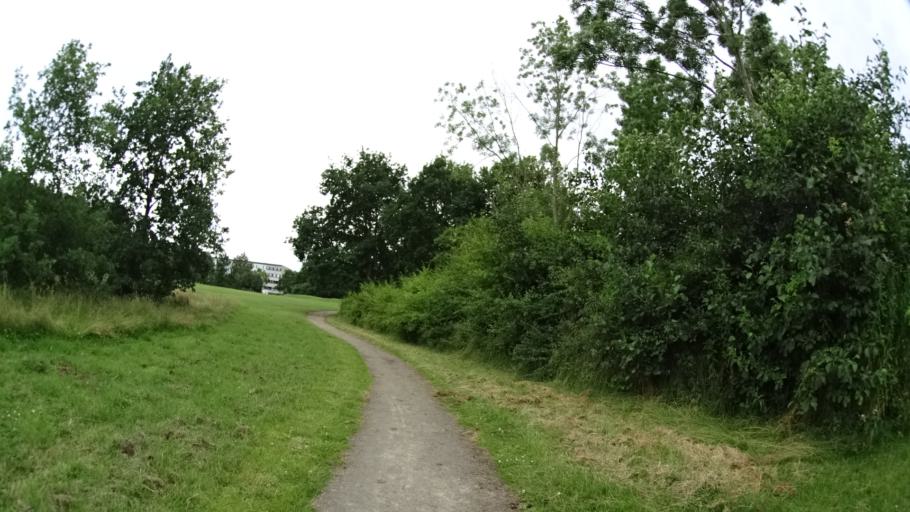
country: DK
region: Central Jutland
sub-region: Arhus Kommune
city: Stavtrup
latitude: 56.1265
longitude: 10.1471
